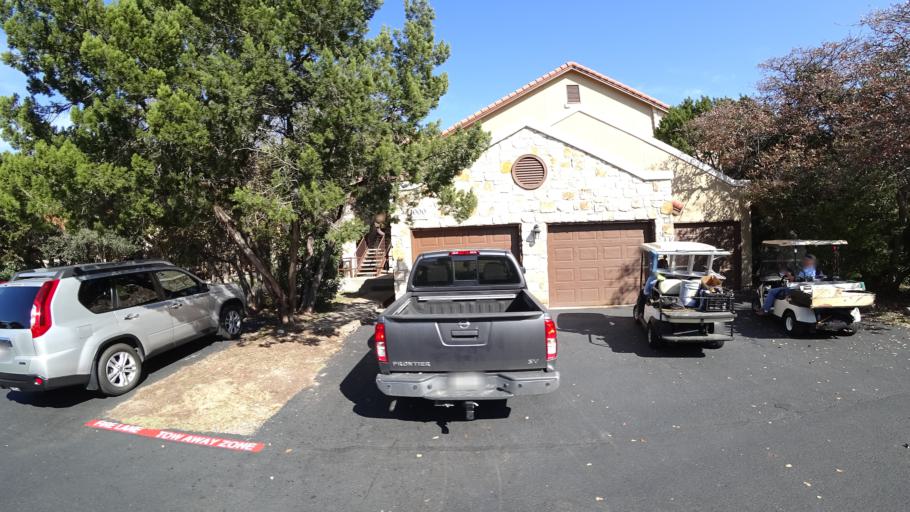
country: US
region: Texas
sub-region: Williamson County
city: Jollyville
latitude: 30.3720
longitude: -97.7610
